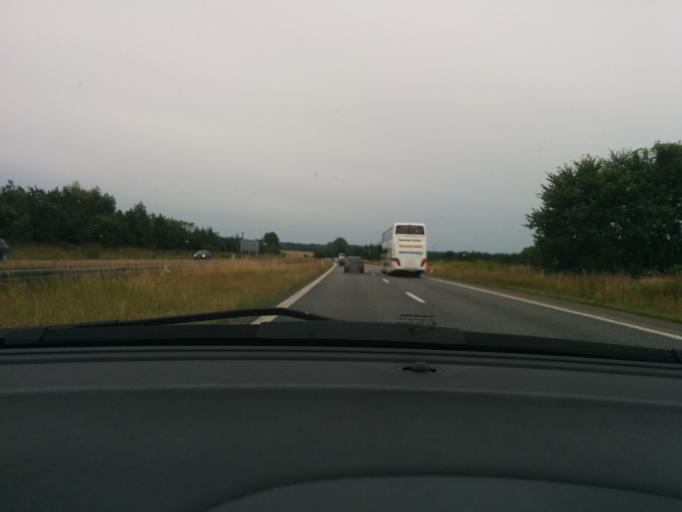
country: DK
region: Zealand
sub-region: Faxe Kommune
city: Ronnede
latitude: 55.2822
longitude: 12.0125
